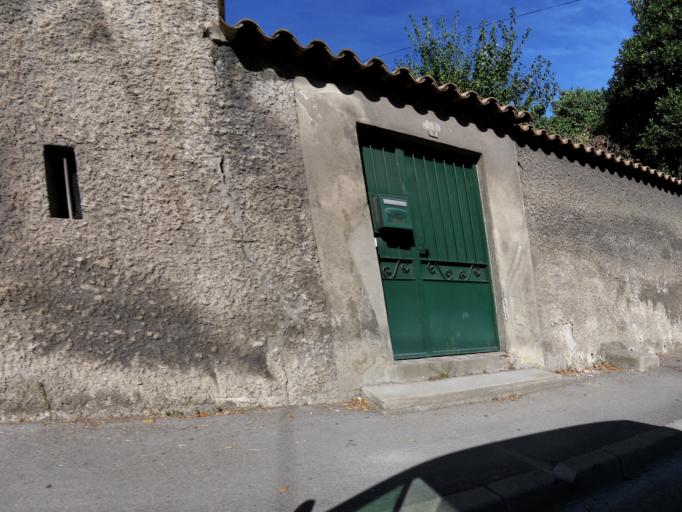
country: FR
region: Languedoc-Roussillon
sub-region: Departement du Gard
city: Nimes
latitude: 43.8395
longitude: 4.3425
